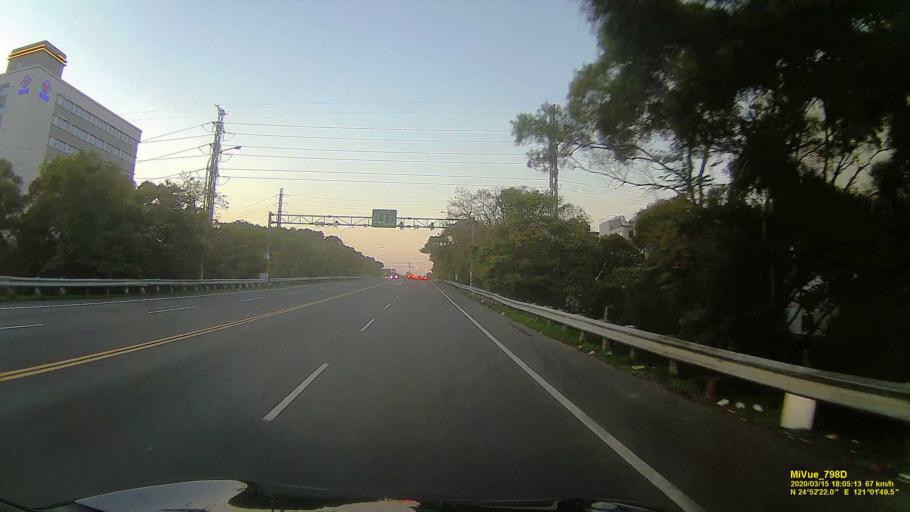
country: TW
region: Taiwan
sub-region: Hsinchu
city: Zhubei
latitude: 24.8731
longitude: 121.0303
